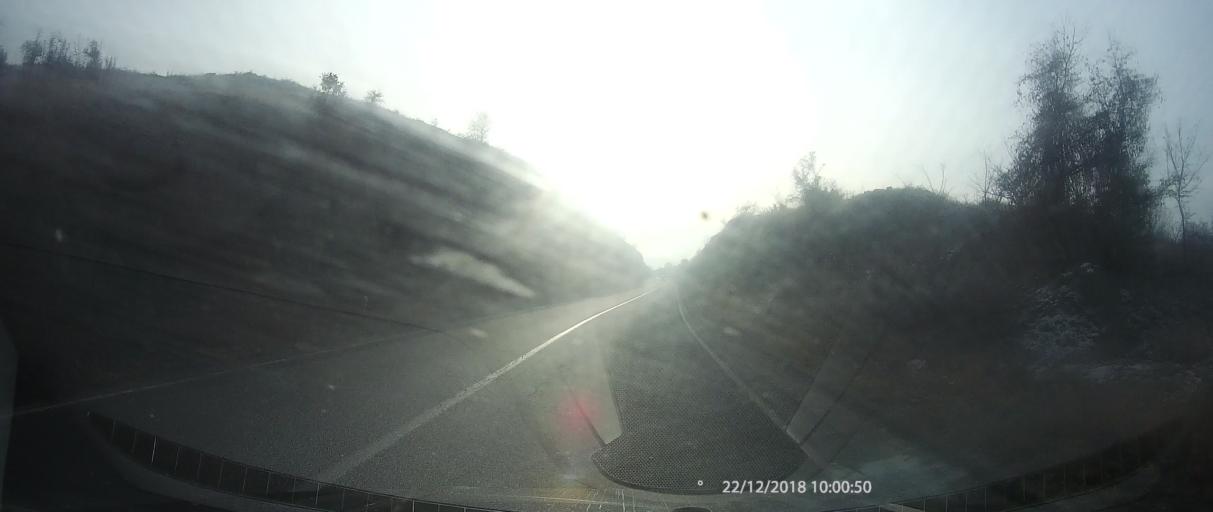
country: MK
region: Opstina Rankovce
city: Rankovce
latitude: 42.1487
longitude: 21.9867
